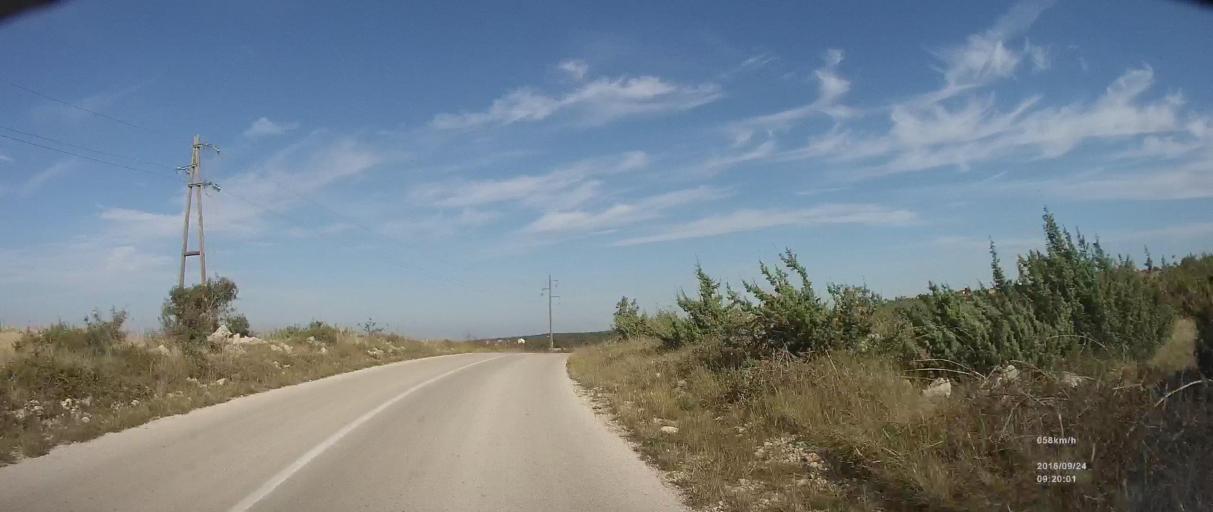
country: HR
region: Zadarska
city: Polaca
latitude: 44.0657
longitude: 15.4994
